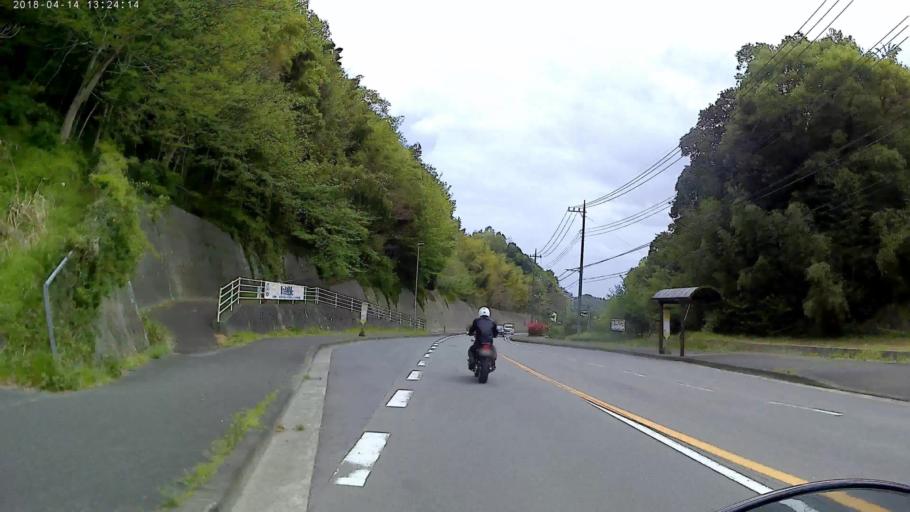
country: JP
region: Kanagawa
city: Hadano
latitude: 35.3347
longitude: 139.2197
